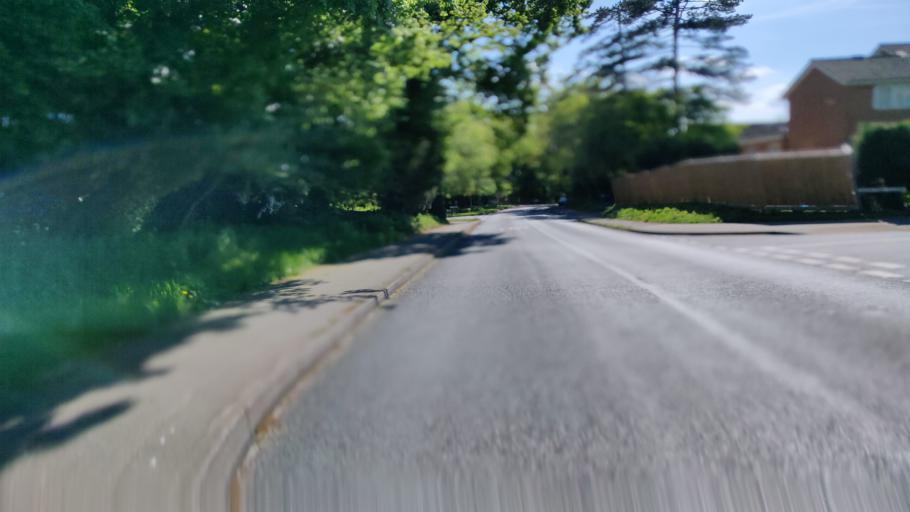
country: GB
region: England
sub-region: West Sussex
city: Rudgwick
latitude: 51.0885
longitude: -0.4503
